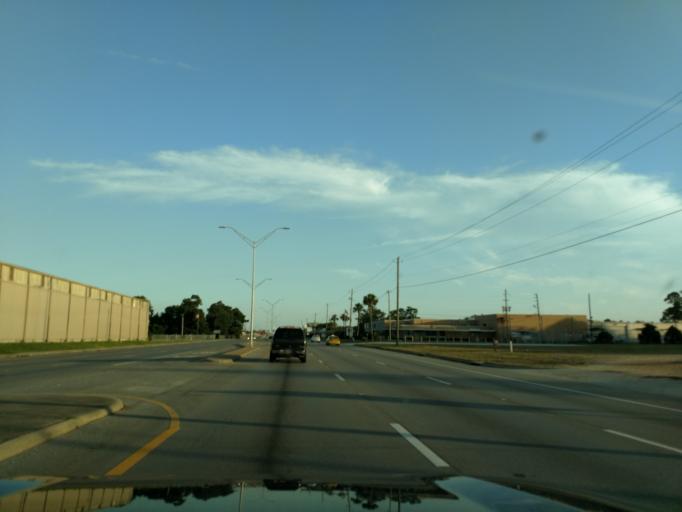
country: US
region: Mississippi
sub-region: Harrison County
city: West Gulfport
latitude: 30.3951
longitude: -89.0932
